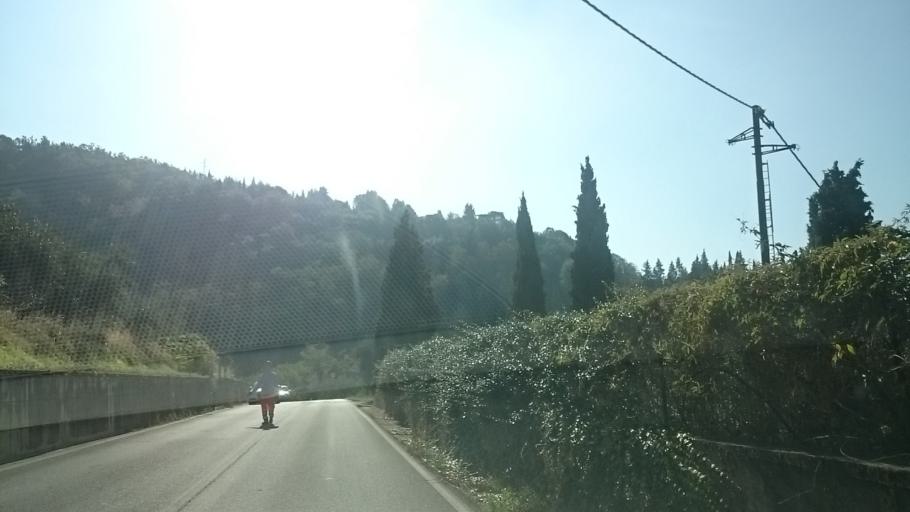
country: IT
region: Tuscany
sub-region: Province of Florence
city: Reggello
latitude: 43.7060
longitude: 11.5229
